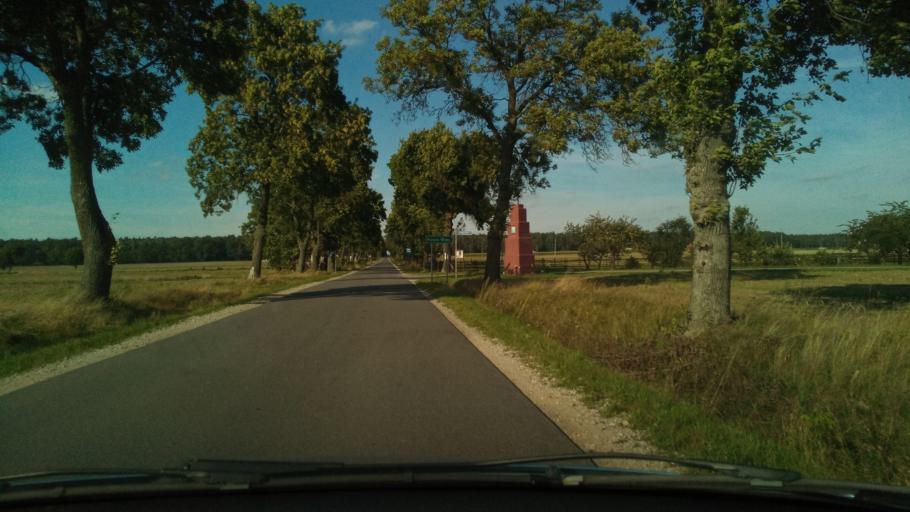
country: PL
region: Lodz Voivodeship
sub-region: Powiat piotrkowski
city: Sulejow
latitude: 51.4013
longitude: 19.8237
